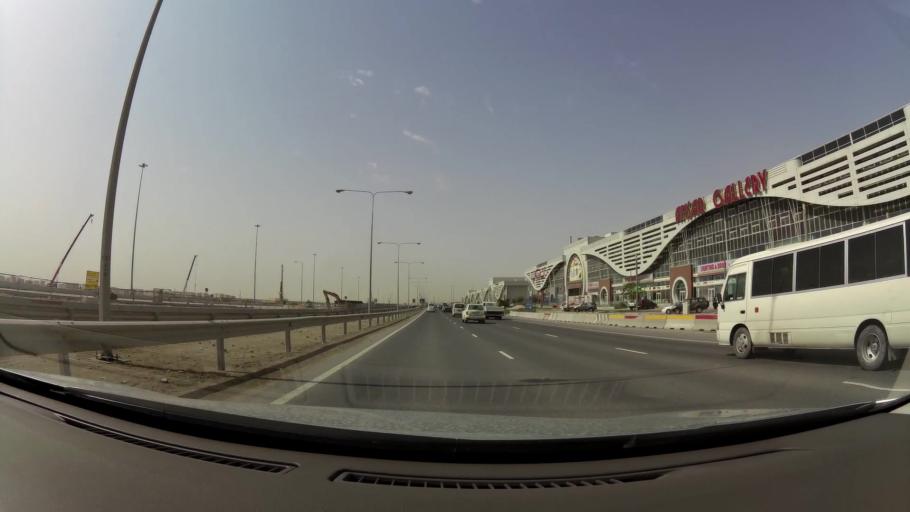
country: QA
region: Baladiyat ad Dawhah
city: Doha
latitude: 25.2172
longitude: 51.5015
